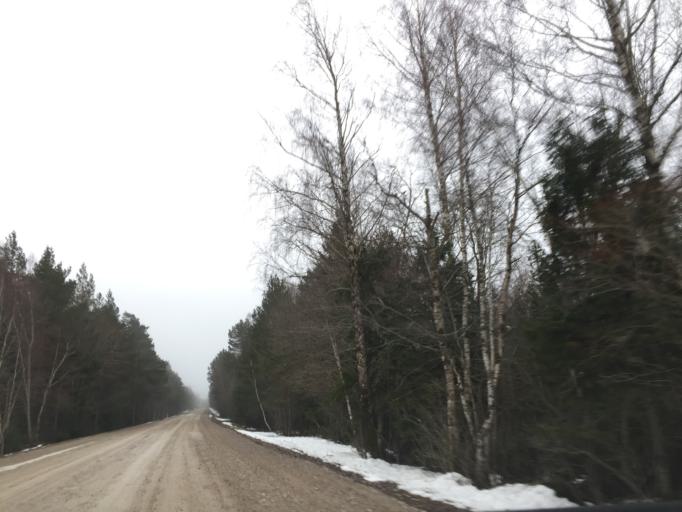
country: EE
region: Saare
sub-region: Kuressaare linn
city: Kuressaare
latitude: 58.4835
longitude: 21.9973
